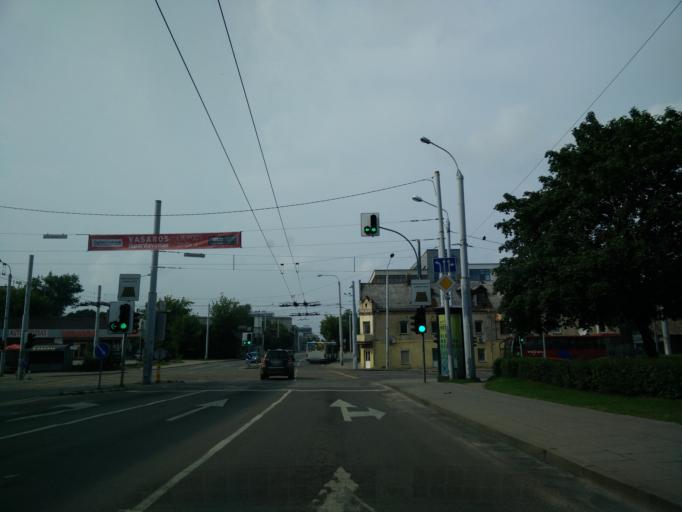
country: LT
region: Vilnius County
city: Naujamiestis
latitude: 54.6715
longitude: 25.2697
